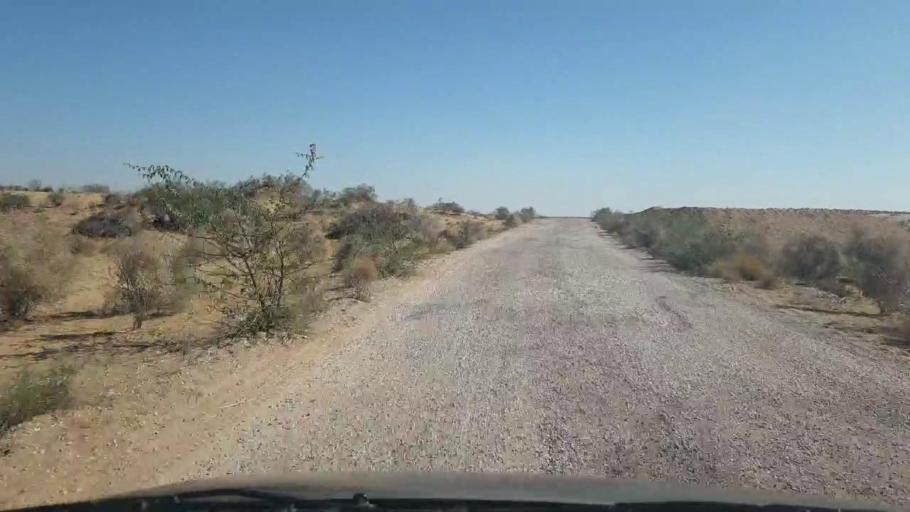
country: PK
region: Sindh
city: Bozdar
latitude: 27.0032
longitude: 68.8410
